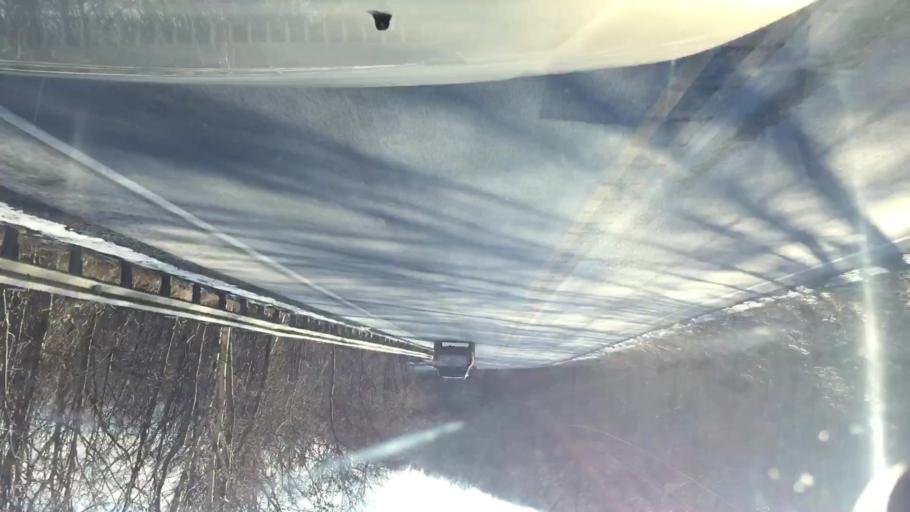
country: US
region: Pennsylvania
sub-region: Luzerne County
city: Conyngham
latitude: 41.0342
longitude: -76.1132
